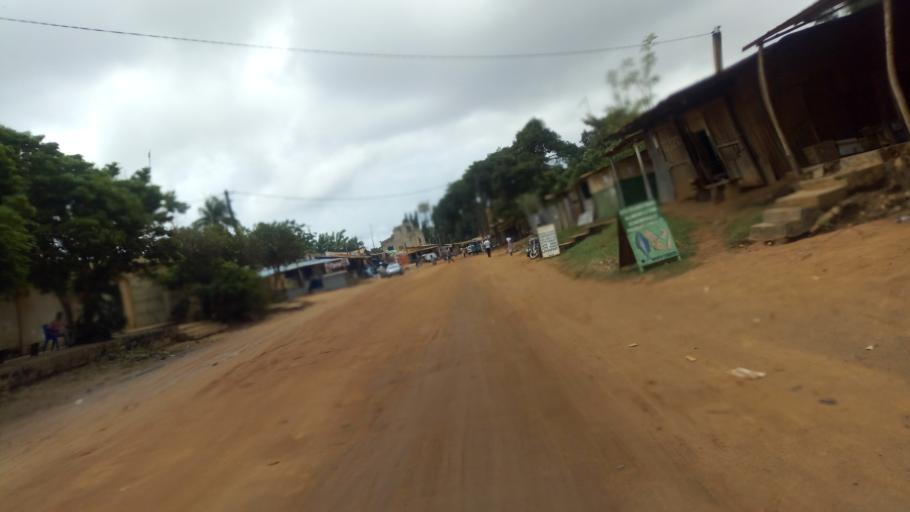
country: TG
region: Maritime
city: Lome
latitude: 6.1801
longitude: 1.1683
